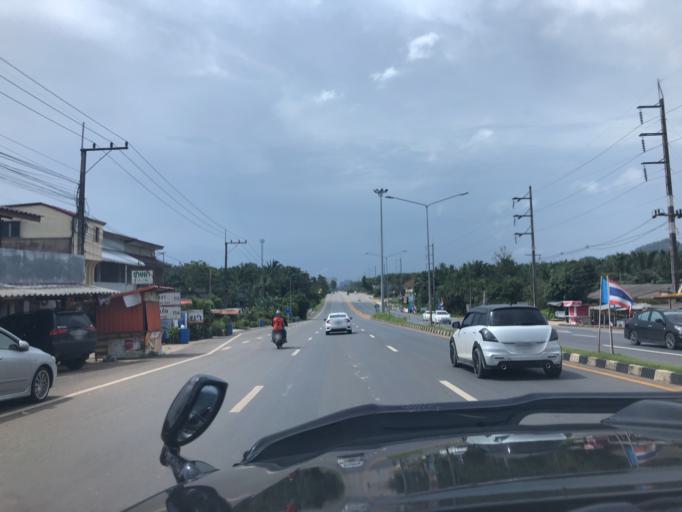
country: TH
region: Phangnga
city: Ban Ao Nang
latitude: 8.2168
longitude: 98.8084
